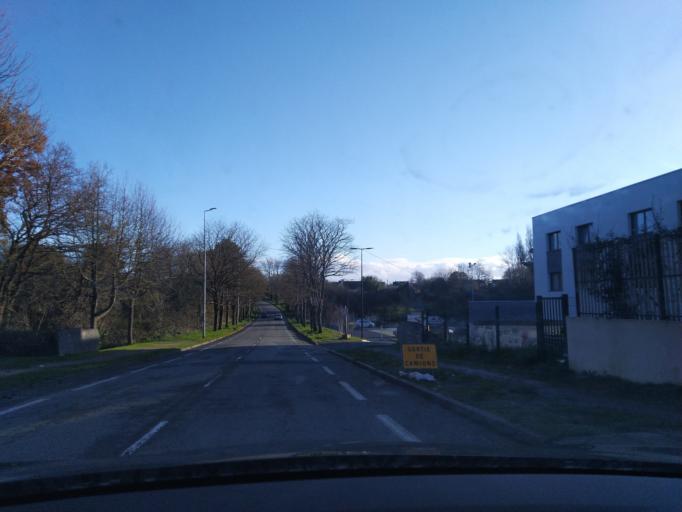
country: FR
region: Brittany
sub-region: Departement du Finistere
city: Morlaix
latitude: 48.5862
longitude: -3.8191
